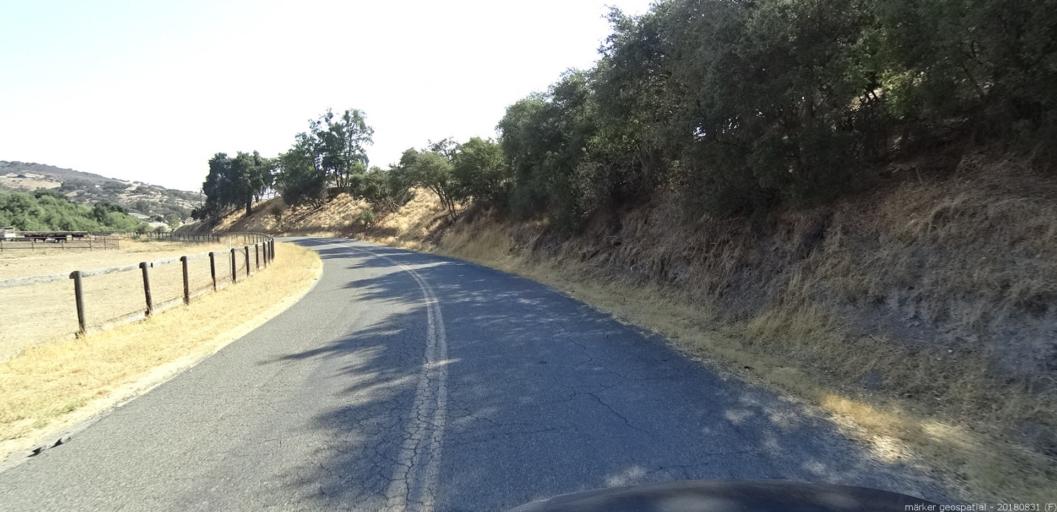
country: US
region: California
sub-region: Monterey County
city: King City
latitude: 36.1530
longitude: -121.1802
